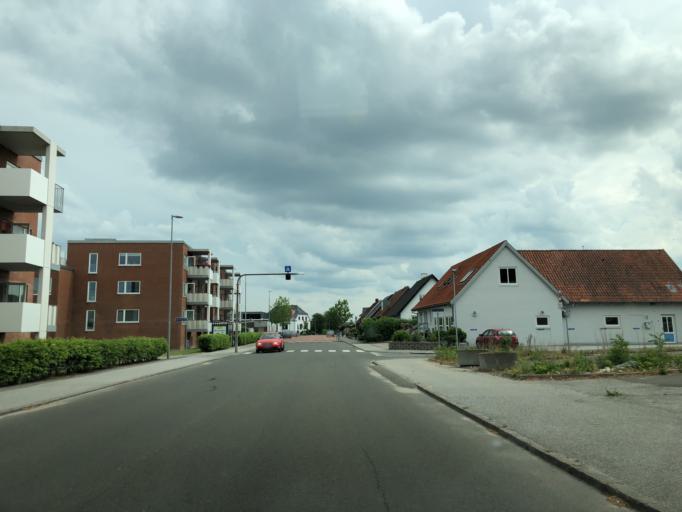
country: DK
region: Central Jutland
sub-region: Struer Kommune
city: Struer
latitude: 56.4909
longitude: 8.5764
